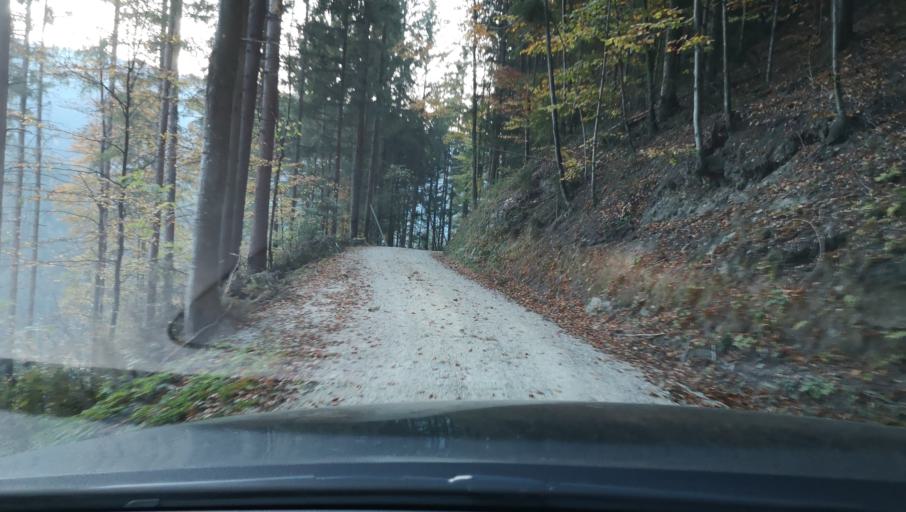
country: AT
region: Styria
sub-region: Politischer Bezirk Weiz
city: Birkfeld
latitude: 47.3616
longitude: 15.6654
